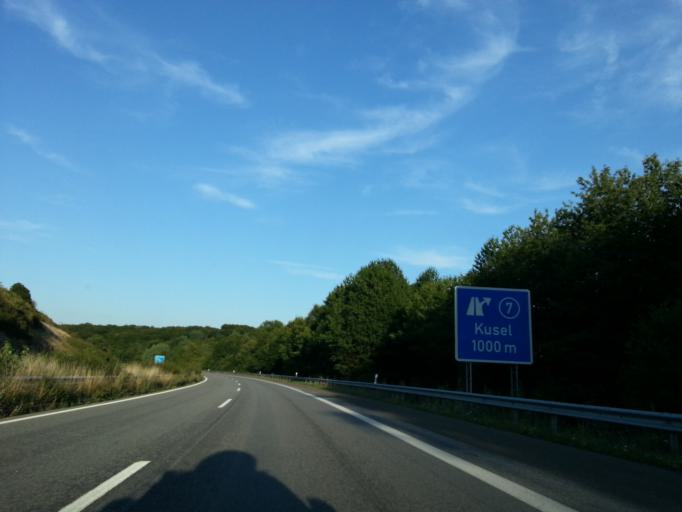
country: DE
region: Rheinland-Pfalz
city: Konken
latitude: 49.5143
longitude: 7.3532
